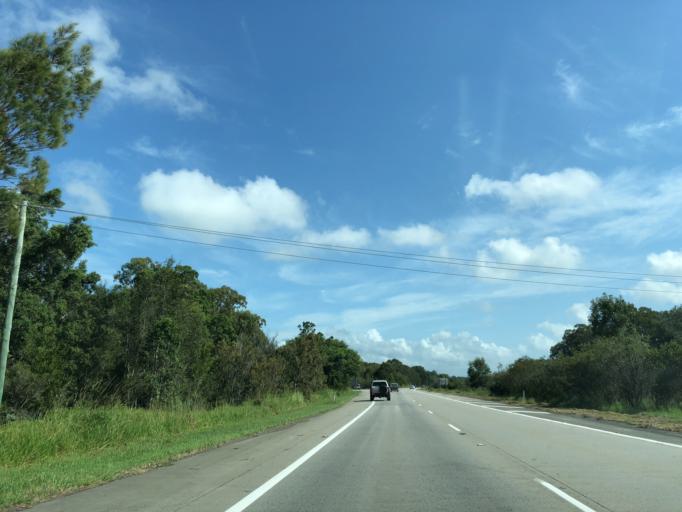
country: AU
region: New South Wales
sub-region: Byron Shire
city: Brunswick Heads
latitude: -28.6007
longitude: 153.5451
